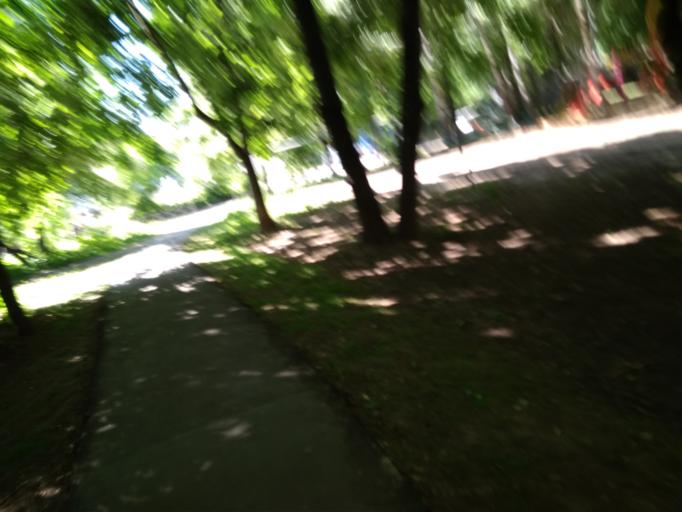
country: RU
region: Moskovskaya
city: Troitsk
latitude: 55.4859
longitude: 37.3004
